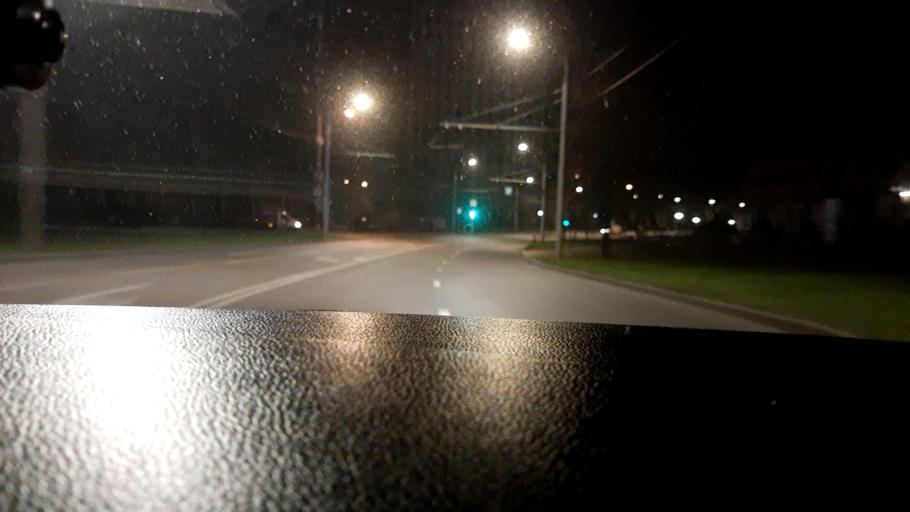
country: RU
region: Moscow
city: Gol'yanovo
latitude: 55.8223
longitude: 37.8041
